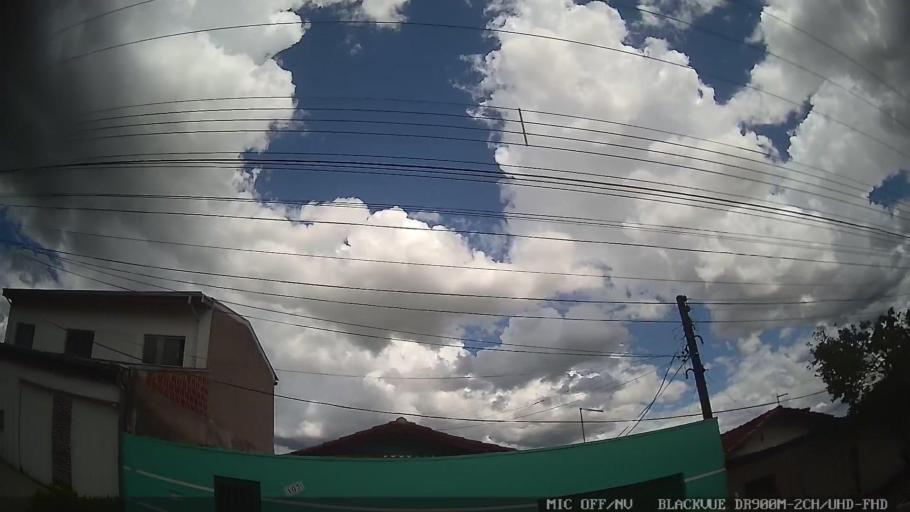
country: BR
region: Sao Paulo
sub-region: Jaguariuna
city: Jaguariuna
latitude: -22.6866
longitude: -46.9951
